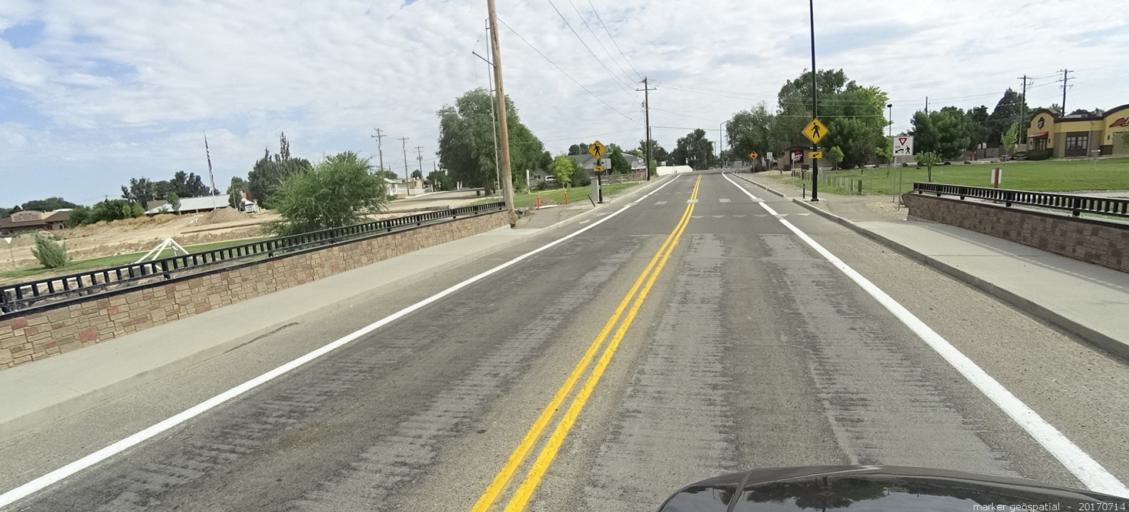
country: US
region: Idaho
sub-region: Ada County
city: Kuna
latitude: 43.4895
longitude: -116.4208
